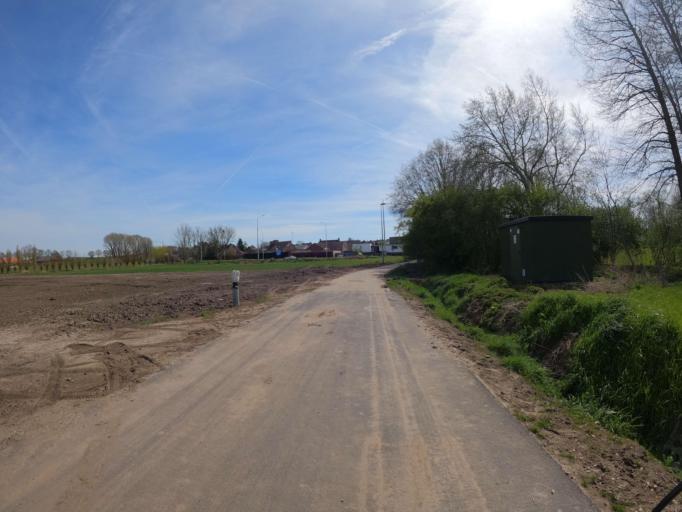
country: BE
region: Flanders
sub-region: Provincie West-Vlaanderen
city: Tielt
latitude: 51.0064
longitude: 3.3317
